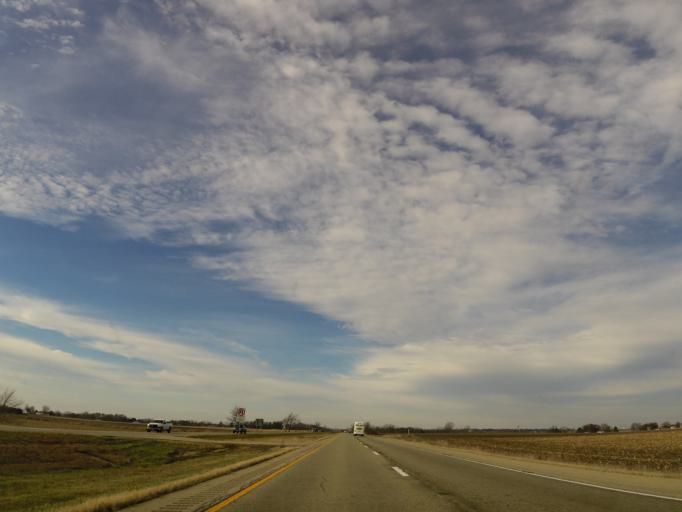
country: US
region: Illinois
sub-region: Woodford County
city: Eureka
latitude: 40.6224
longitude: -89.2870
